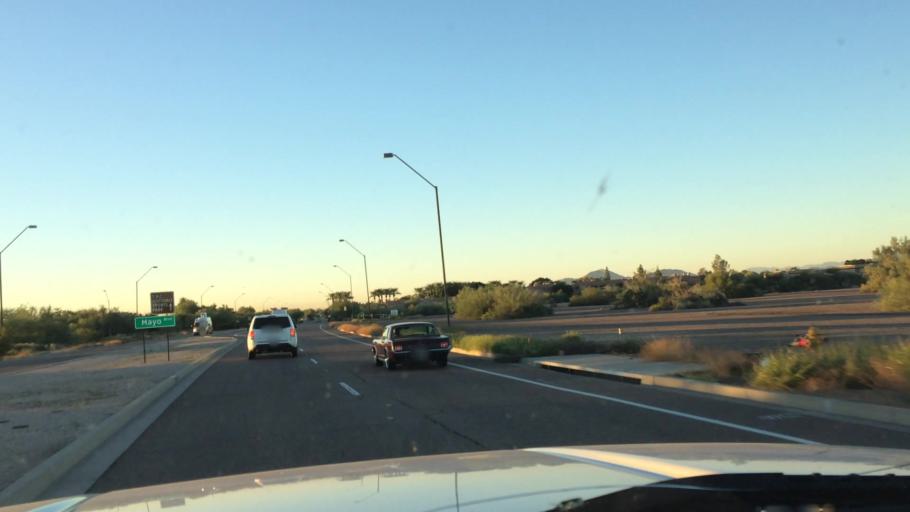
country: US
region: Arizona
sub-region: Maricopa County
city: Paradise Valley
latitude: 33.6518
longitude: -111.9087
